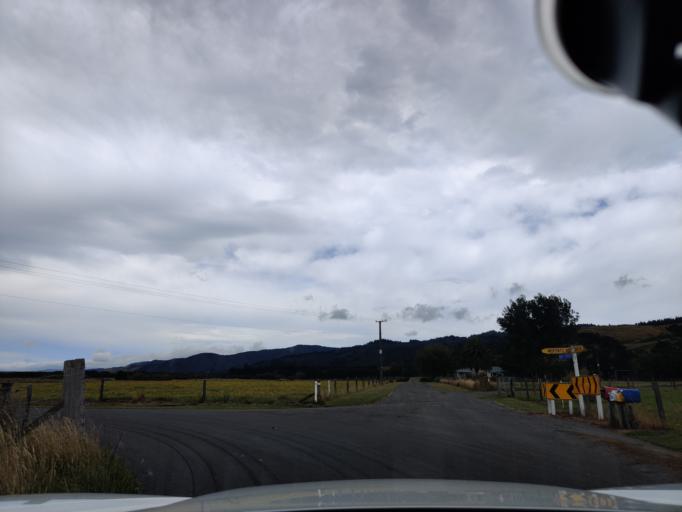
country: NZ
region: Wellington
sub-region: Masterton District
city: Masterton
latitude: -41.0295
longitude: 175.4465
